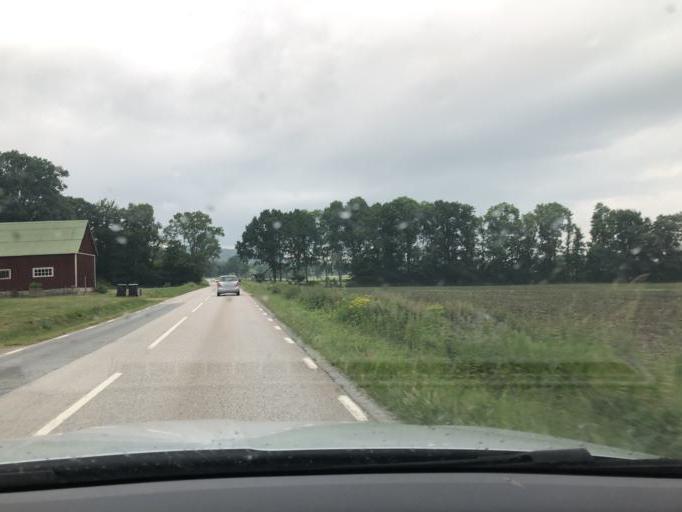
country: SE
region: Blekinge
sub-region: Solvesborgs Kommun
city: Soelvesborg
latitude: 56.0822
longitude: 14.6076
